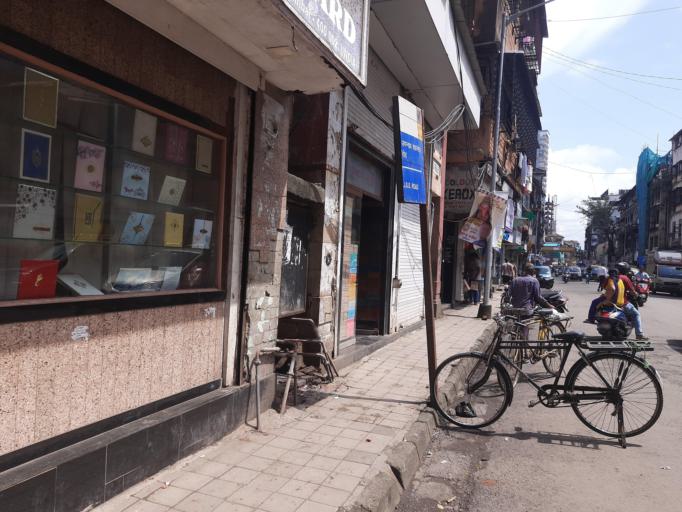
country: IN
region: Maharashtra
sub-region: Raigarh
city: Uran
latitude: 18.9490
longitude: 72.8254
